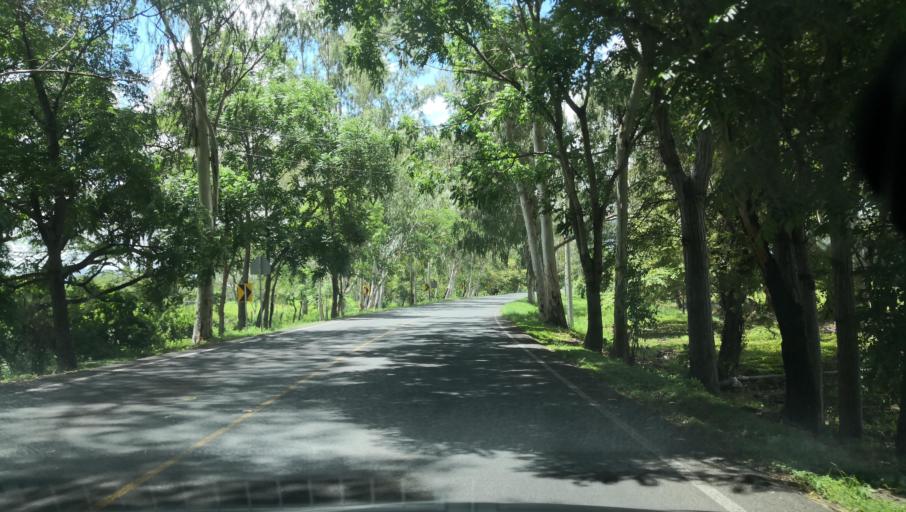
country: NI
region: Esteli
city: Condega
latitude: 13.2474
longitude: -86.3712
